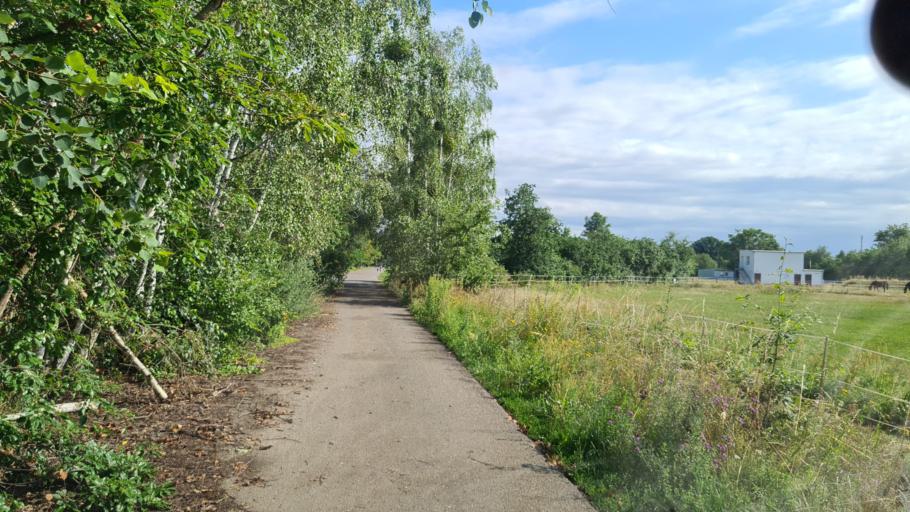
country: DE
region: Brandenburg
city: Senftenberg
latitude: 51.5462
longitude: 14.0518
